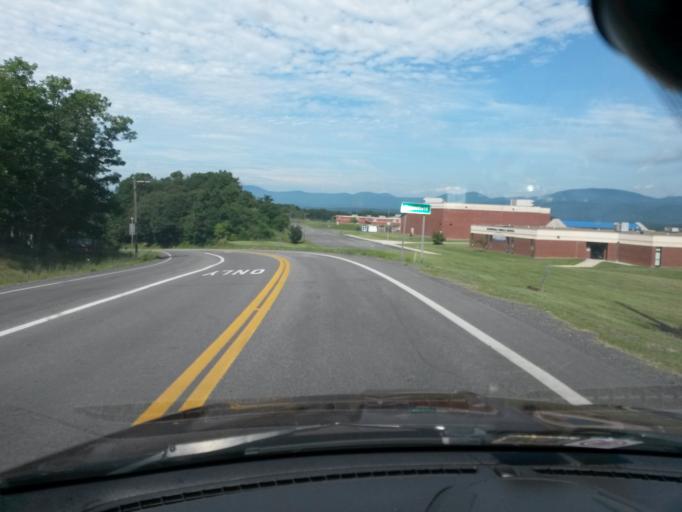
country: US
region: West Virginia
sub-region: Hardy County
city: Moorefield
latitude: 39.0685
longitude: -78.9437
